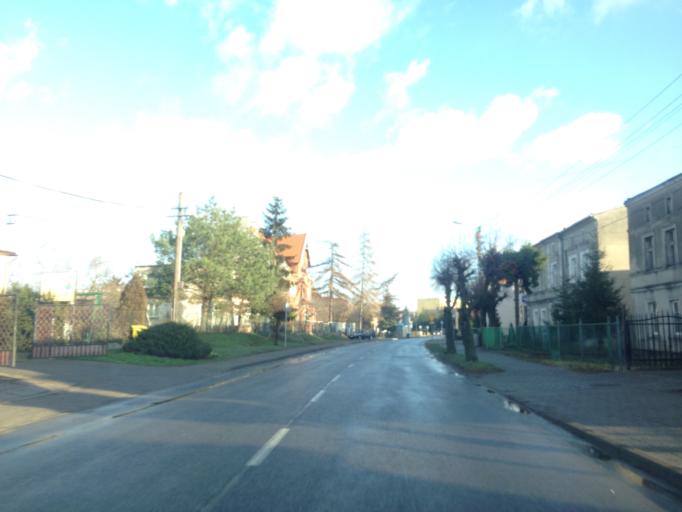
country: PL
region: Kujawsko-Pomorskie
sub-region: Powiat grudziadzki
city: Lasin
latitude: 53.5167
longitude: 19.0800
